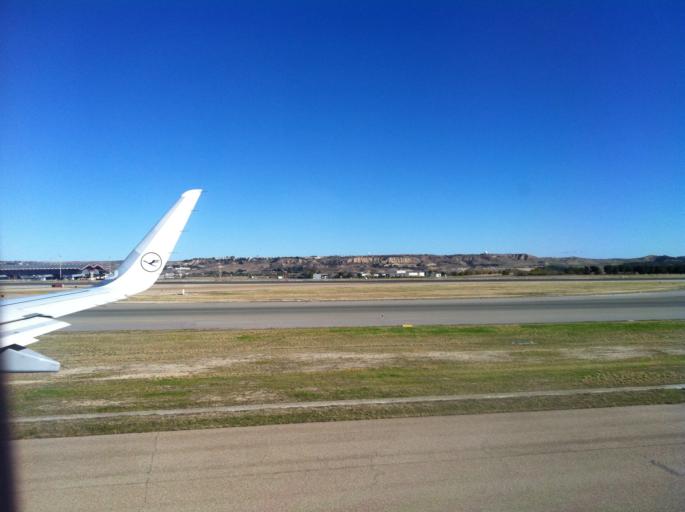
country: ES
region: Madrid
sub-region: Provincia de Madrid
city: Barajas de Madrid
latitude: 40.4823
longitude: -3.5774
